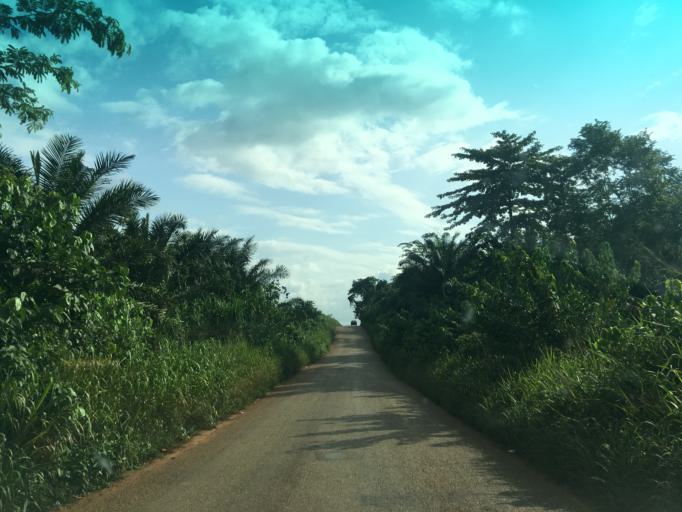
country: GH
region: Western
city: Bibiani
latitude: 6.7679
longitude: -2.5731
